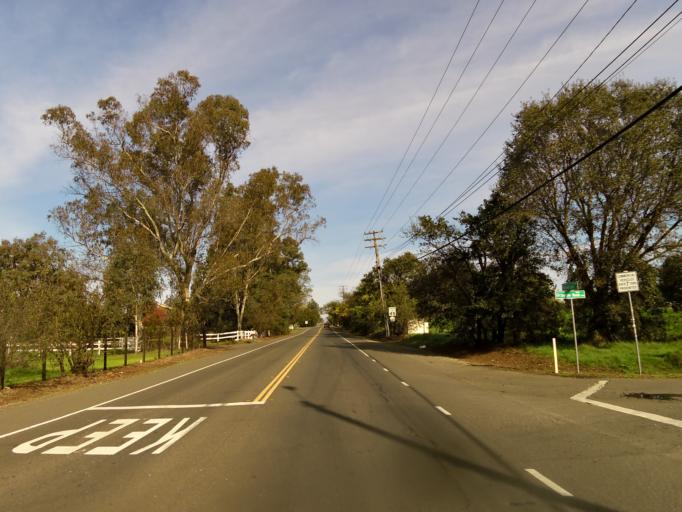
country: US
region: California
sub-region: Sacramento County
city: Wilton
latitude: 38.4378
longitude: -121.2930
